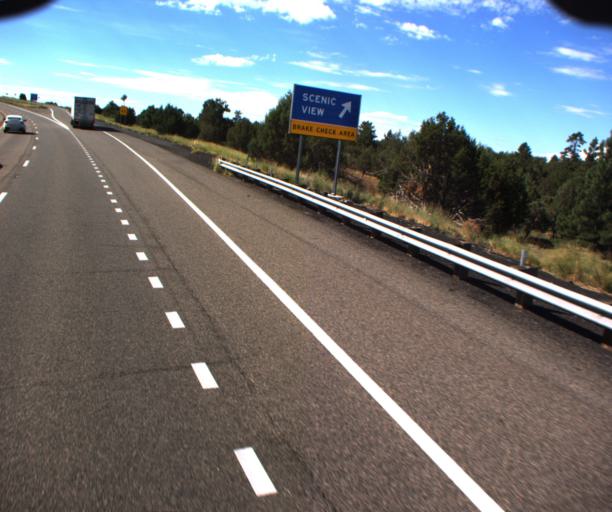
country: US
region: Arizona
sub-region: Yavapai County
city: Village of Oak Creek (Big Park)
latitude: 34.8165
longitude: -111.6132
